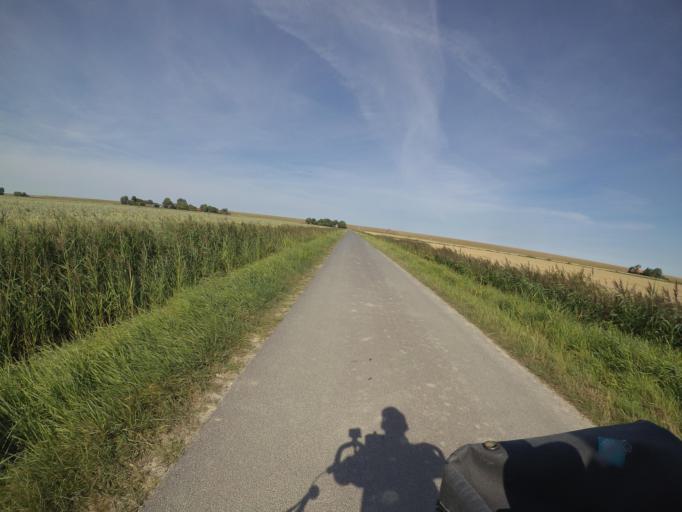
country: NL
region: Friesland
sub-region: Gemeente Ferwerderadiel
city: Marrum
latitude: 53.3407
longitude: 5.8013
